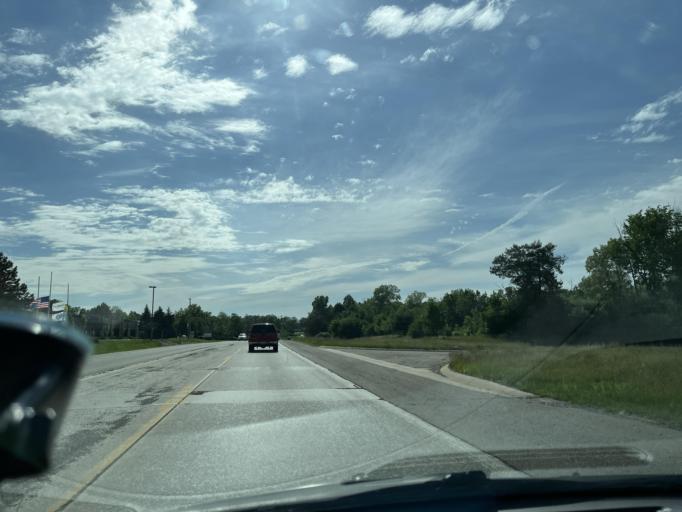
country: US
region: Michigan
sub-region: Barry County
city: Hastings
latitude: 42.6462
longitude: -85.3216
